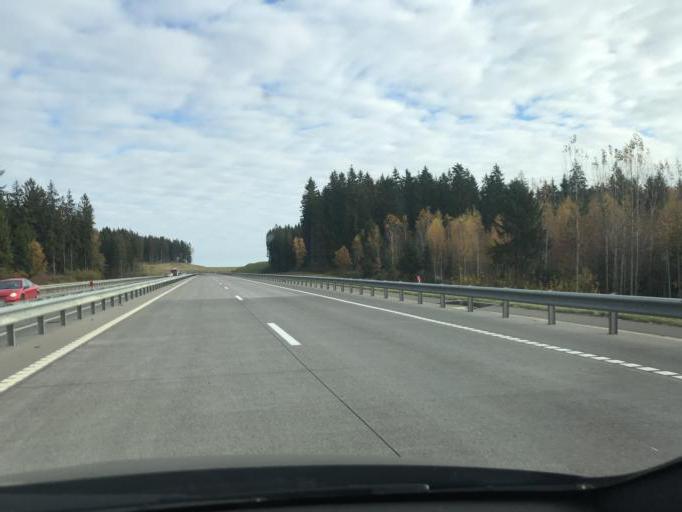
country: BY
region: Minsk
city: Pyatryshki
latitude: 54.0679
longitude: 27.2519
